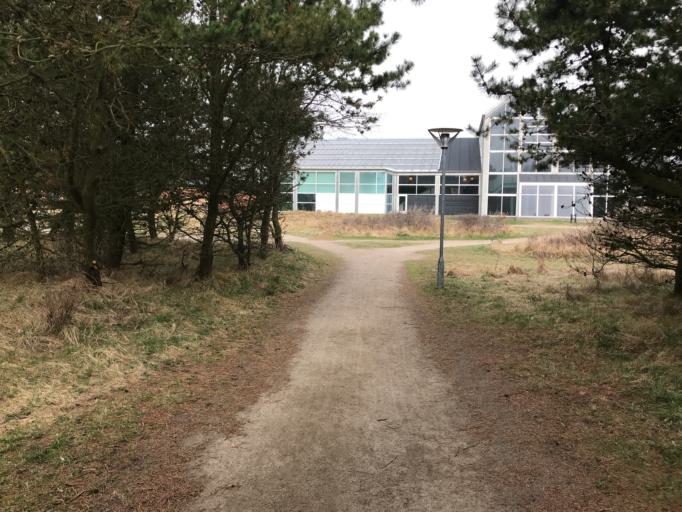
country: DK
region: North Denmark
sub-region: Hjorring Kommune
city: Hjorring
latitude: 57.4926
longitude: 9.8374
